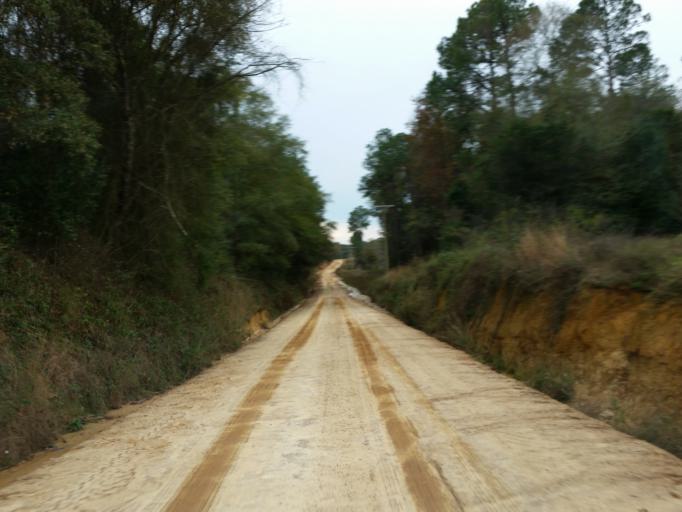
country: US
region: Georgia
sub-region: Crisp County
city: Cordele
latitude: 31.8716
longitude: -83.7276
